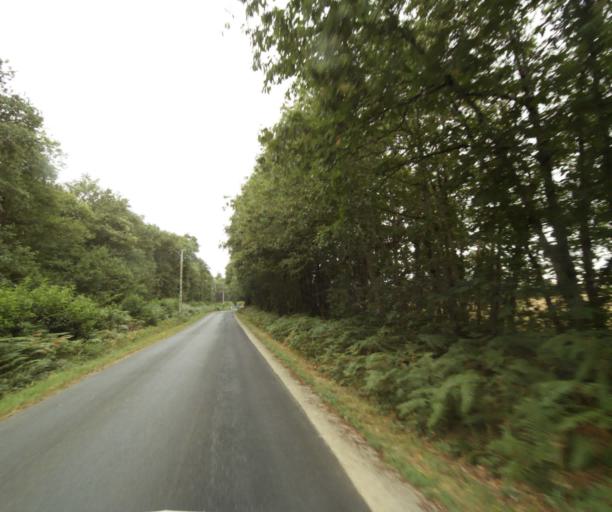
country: FR
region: Pays de la Loire
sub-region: Departement de la Sarthe
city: Sable-sur-Sarthe
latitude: 47.8133
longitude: -0.3538
